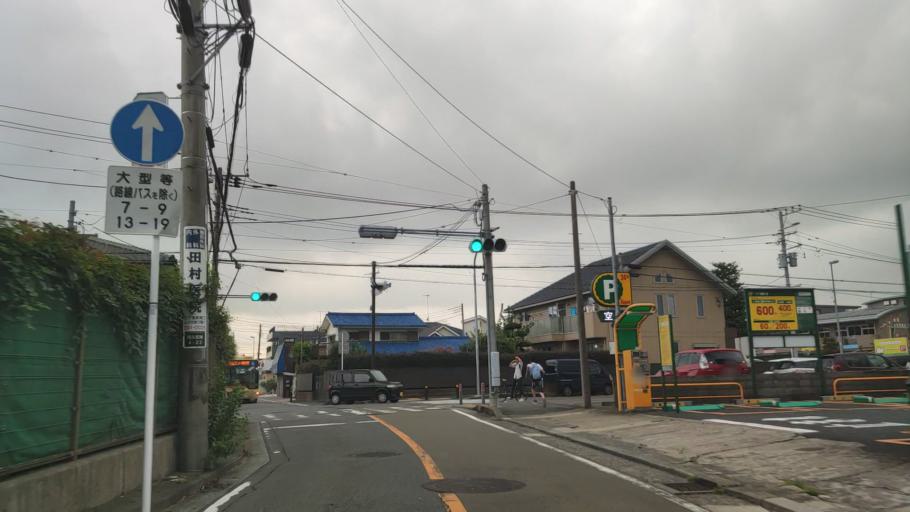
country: JP
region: Kanagawa
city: Minami-rinkan
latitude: 35.4491
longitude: 139.4994
